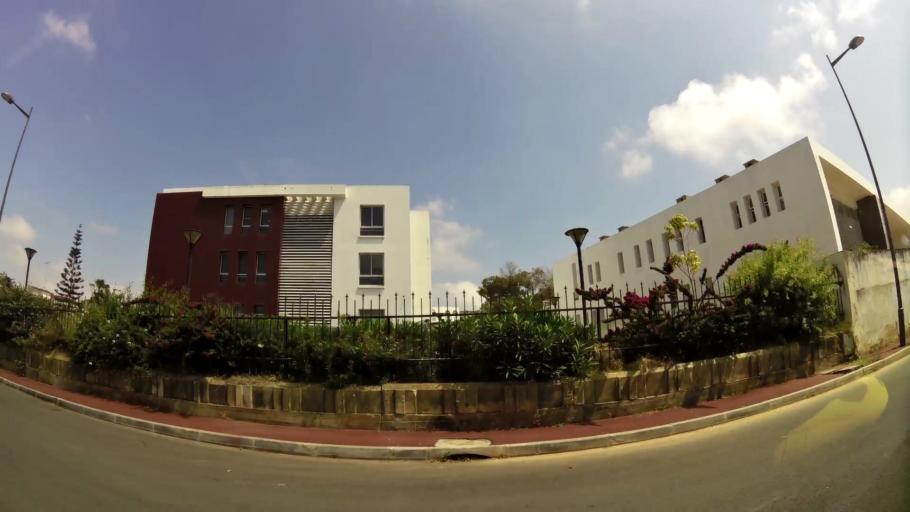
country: MA
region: Rabat-Sale-Zemmour-Zaer
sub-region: Skhirate-Temara
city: Temara
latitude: 33.9638
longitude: -6.8776
